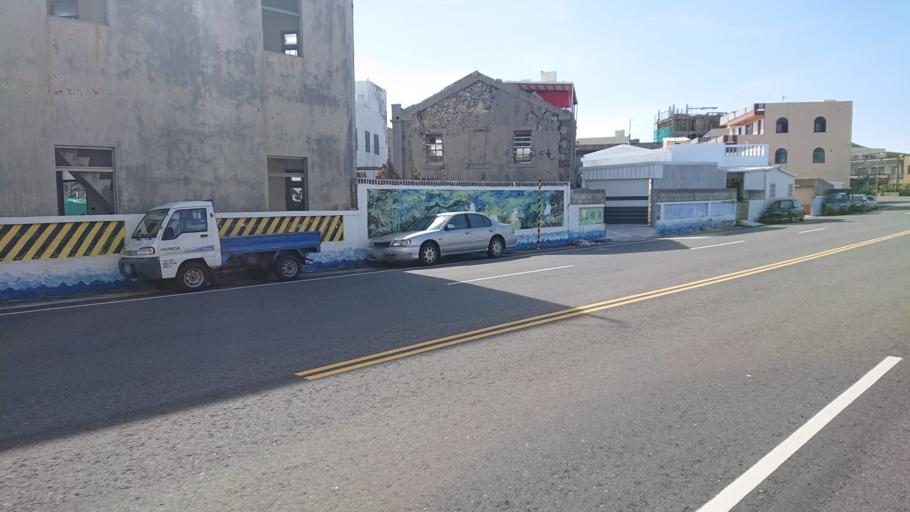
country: TW
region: Taiwan
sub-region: Penghu
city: Ma-kung
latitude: 23.5252
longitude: 119.5712
